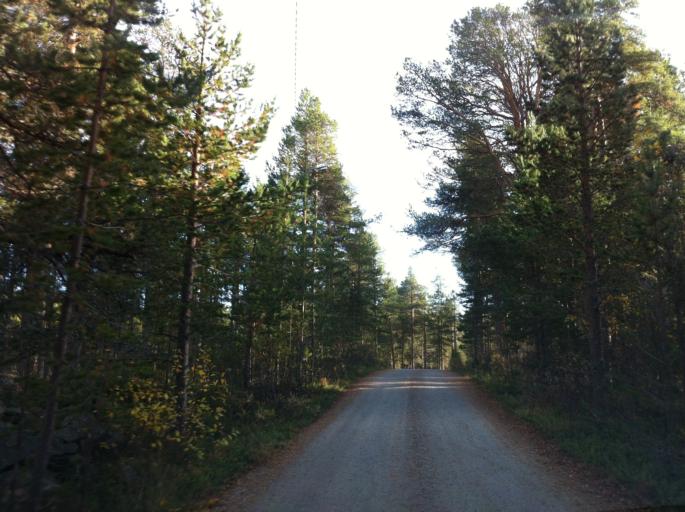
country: NO
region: Hedmark
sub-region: Engerdal
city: Engerdal
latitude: 62.1709
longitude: 11.9432
